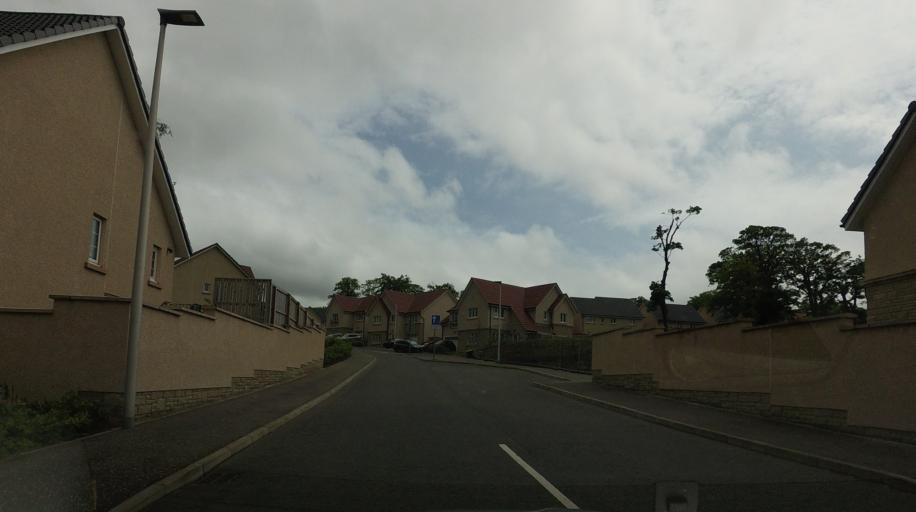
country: GB
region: Scotland
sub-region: Edinburgh
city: Ratho
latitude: 55.9206
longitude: -3.3942
